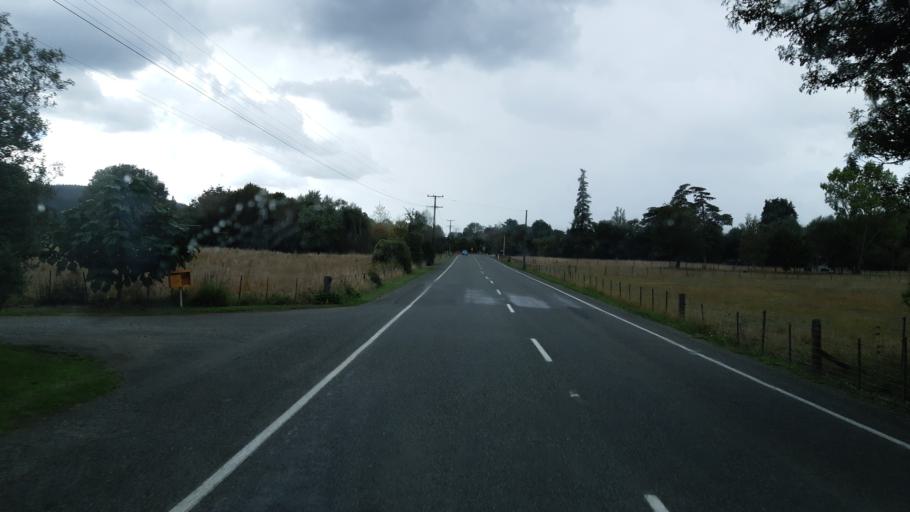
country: NZ
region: Tasman
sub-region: Tasman District
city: Wakefield
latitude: -41.4095
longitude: 173.0267
